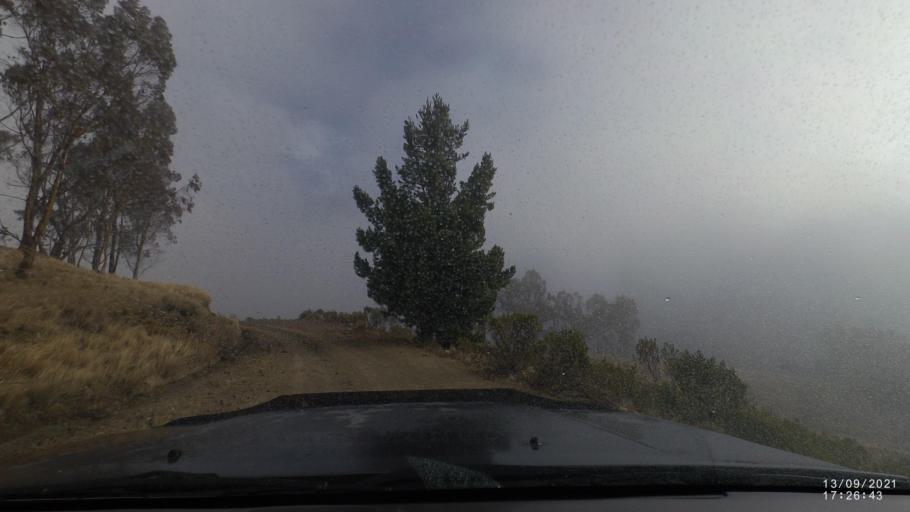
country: BO
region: Cochabamba
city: Colomi
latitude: -17.3592
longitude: -65.7858
